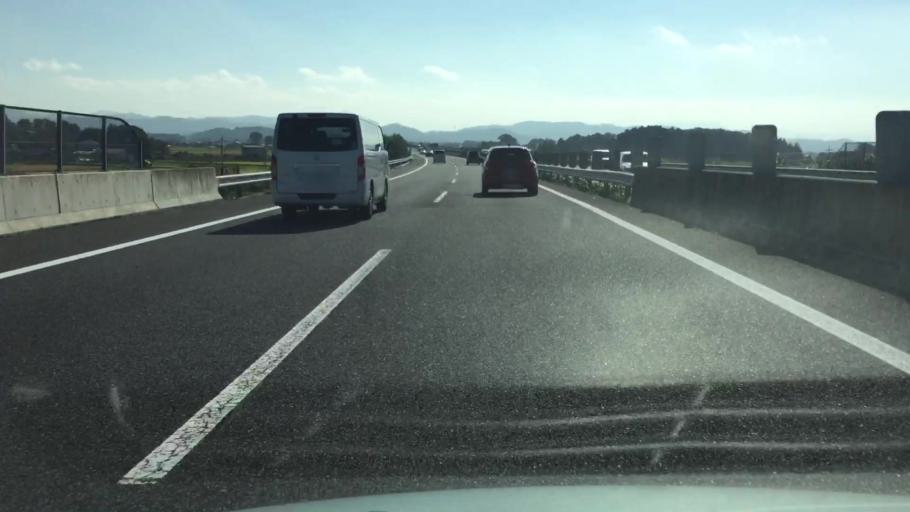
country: JP
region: Tochigi
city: Mooka
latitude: 36.4221
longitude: 139.9834
